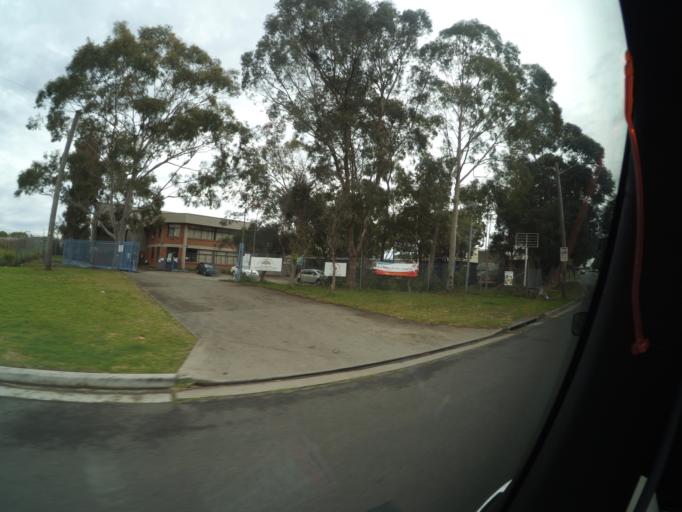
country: AU
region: New South Wales
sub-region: Bankstown
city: Regents Park
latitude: -33.8869
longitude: 151.0230
